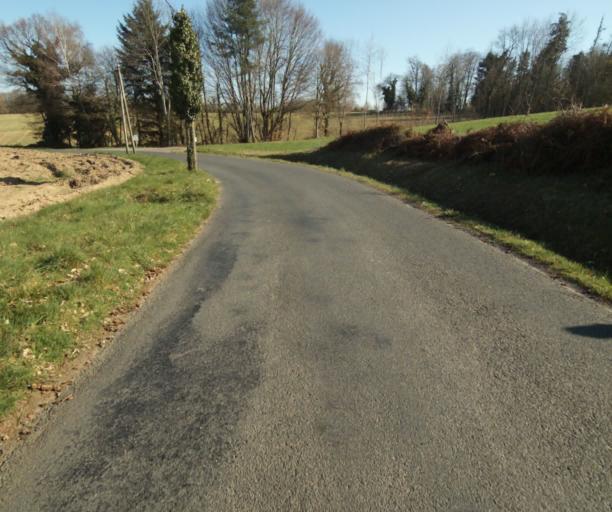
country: FR
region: Limousin
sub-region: Departement de la Correze
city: Saint-Clement
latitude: 45.2940
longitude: 1.7003
